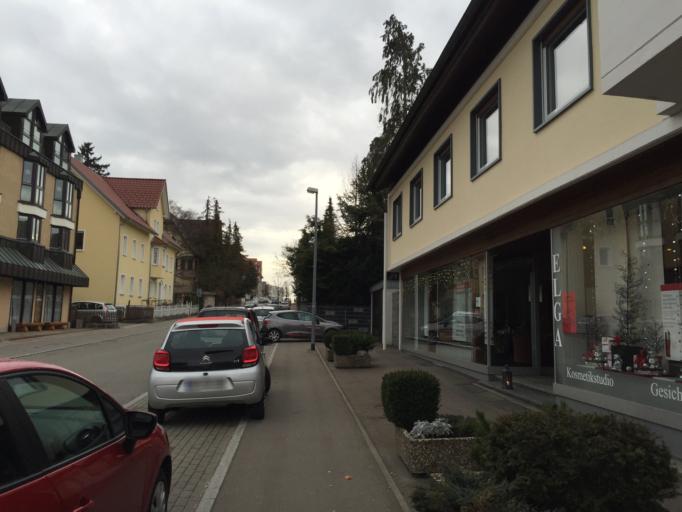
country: DE
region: Baden-Wuerttemberg
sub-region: Freiburg Region
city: Trossingen
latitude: 48.0750
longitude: 8.6352
